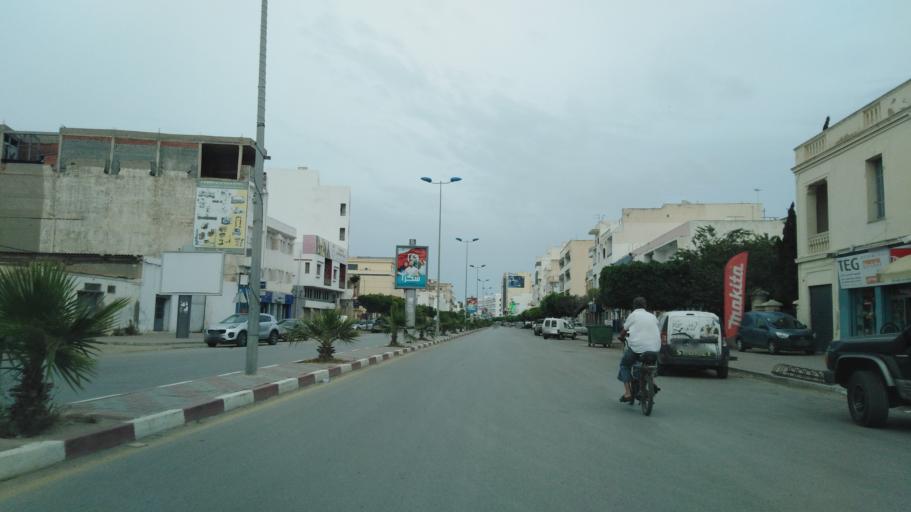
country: TN
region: Safaqis
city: Sfax
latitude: 34.7335
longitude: 10.7523
